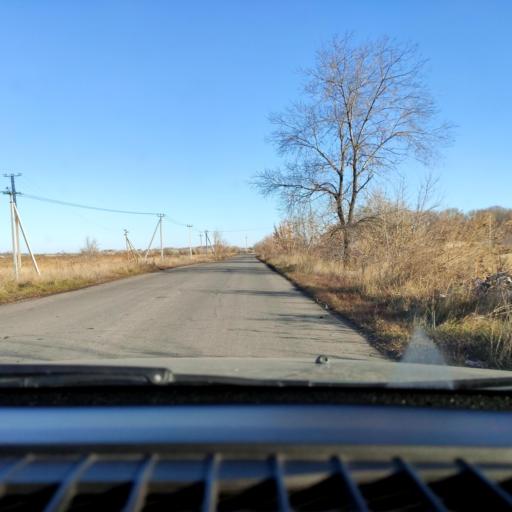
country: RU
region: Samara
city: Tol'yatti
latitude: 53.6472
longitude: 49.3194
